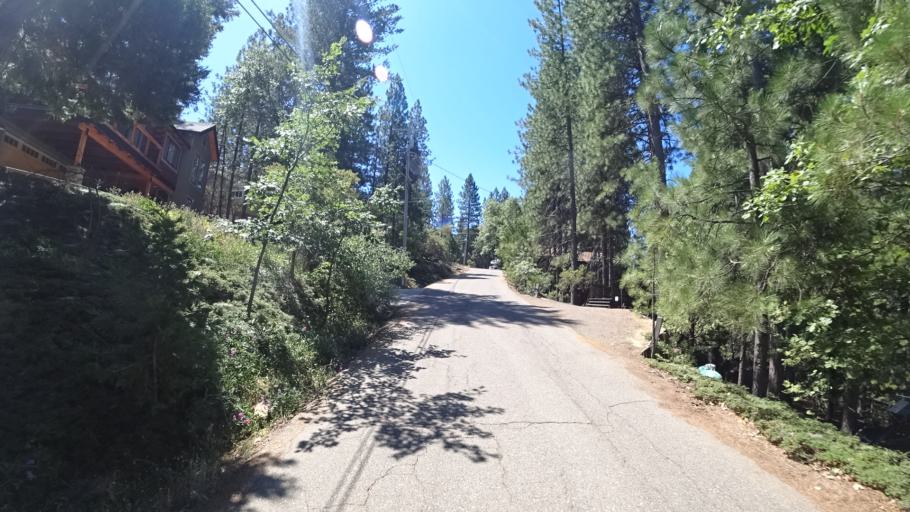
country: US
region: California
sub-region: Calaveras County
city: Arnold
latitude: 38.2266
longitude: -120.3771
